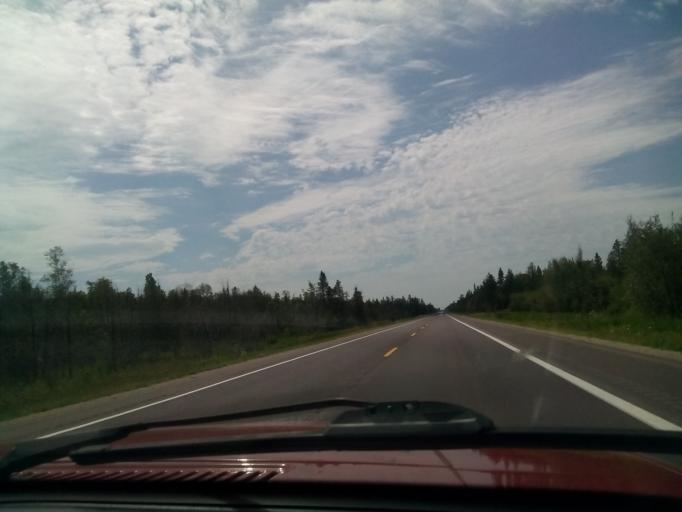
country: US
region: Michigan
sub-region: Schoolcraft County
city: Manistique
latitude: 46.0373
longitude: -85.9755
